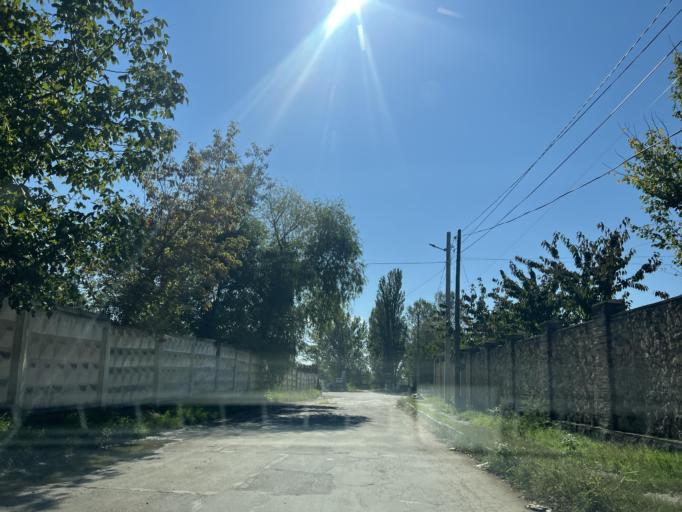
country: RO
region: Iasi
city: Ungheni-Prut
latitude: 47.1946
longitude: 27.7977
